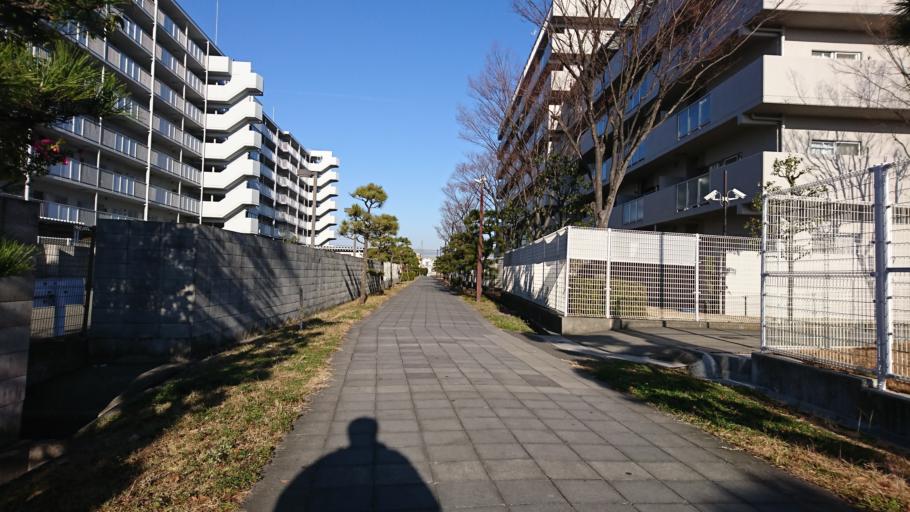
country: JP
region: Hyogo
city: Kakogawacho-honmachi
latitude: 34.7496
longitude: 134.8388
